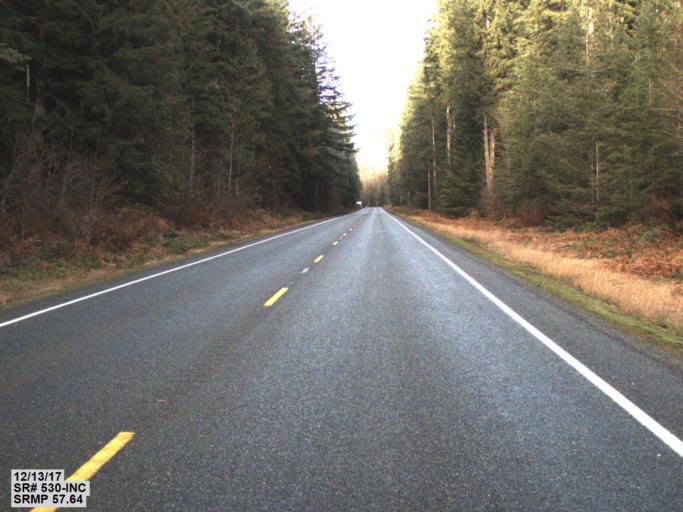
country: US
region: Washington
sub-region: Snohomish County
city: Darrington
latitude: 48.3598
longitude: -121.5398
